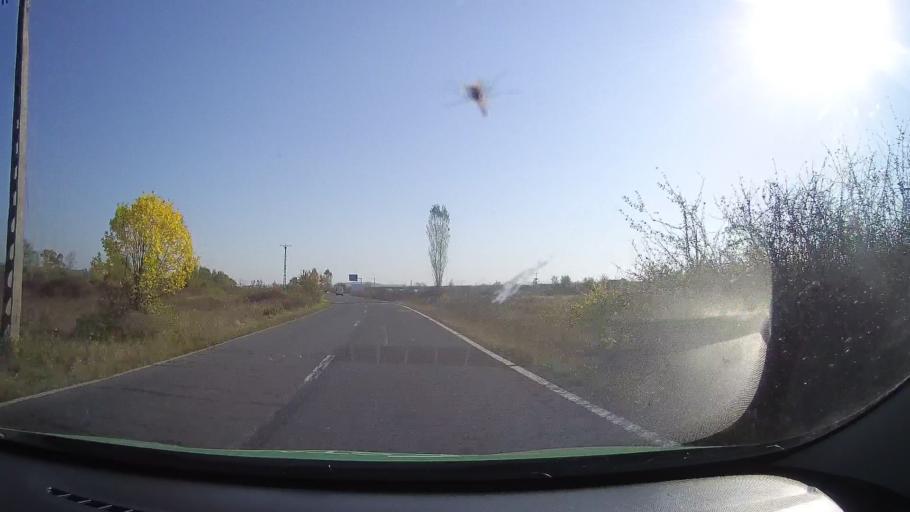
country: RO
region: Timis
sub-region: Comuna Margina
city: Margina
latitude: 45.8576
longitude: 22.2355
